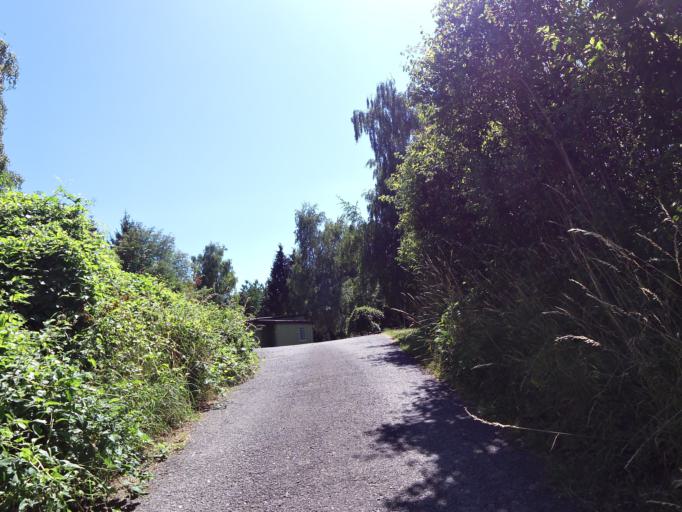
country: DE
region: Bavaria
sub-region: Regierungsbezirk Unterfranken
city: Gerbrunn
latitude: 49.7659
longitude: 9.9972
